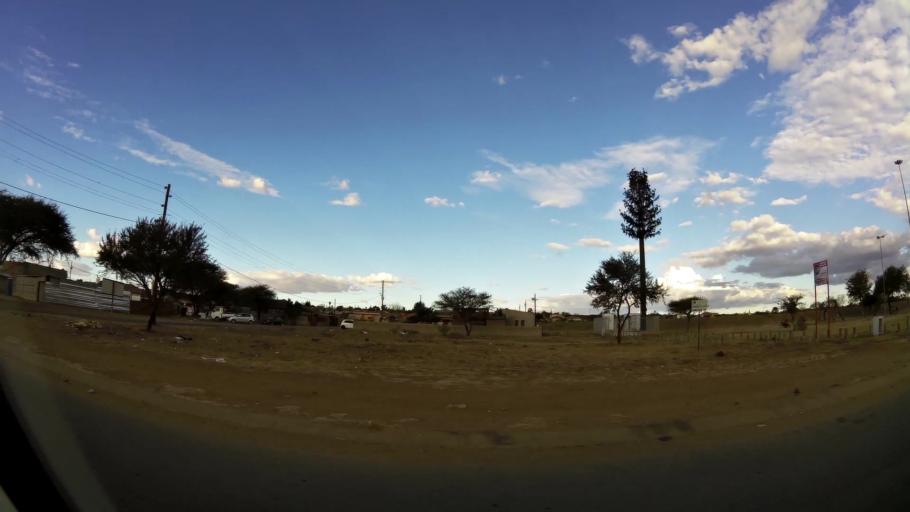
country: ZA
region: Limpopo
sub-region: Capricorn District Municipality
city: Polokwane
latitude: -23.9168
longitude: 29.4222
